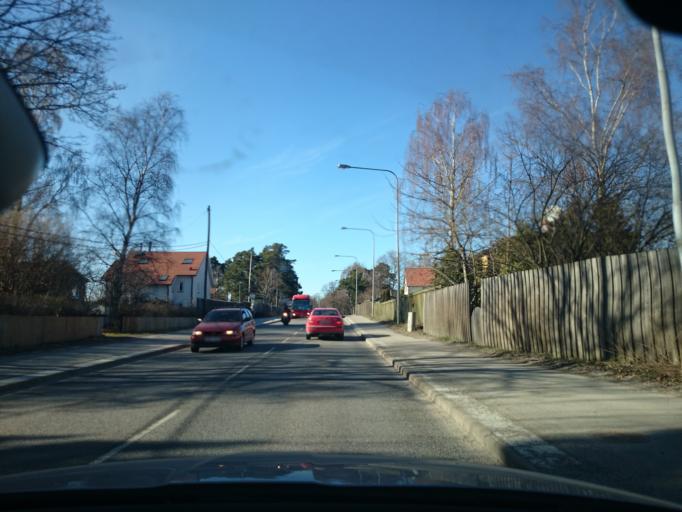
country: SE
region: Stockholm
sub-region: Huddinge Kommun
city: Segeltorp
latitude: 59.2737
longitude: 17.9511
